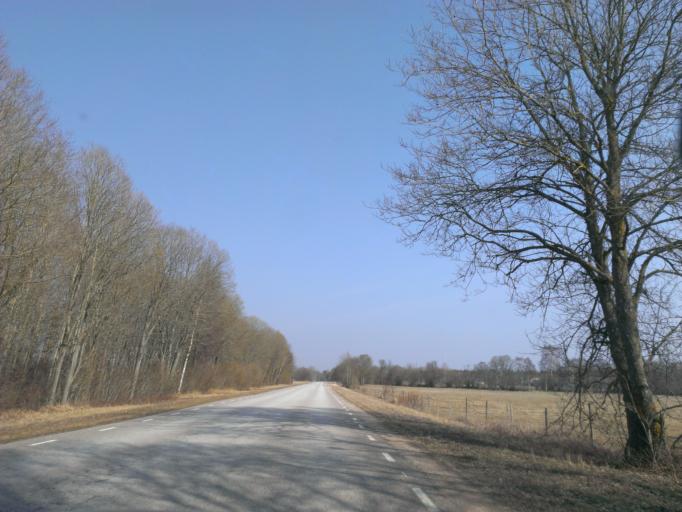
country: EE
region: Saare
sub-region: Kuressaare linn
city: Kuressaare
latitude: 58.2911
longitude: 22.6658
